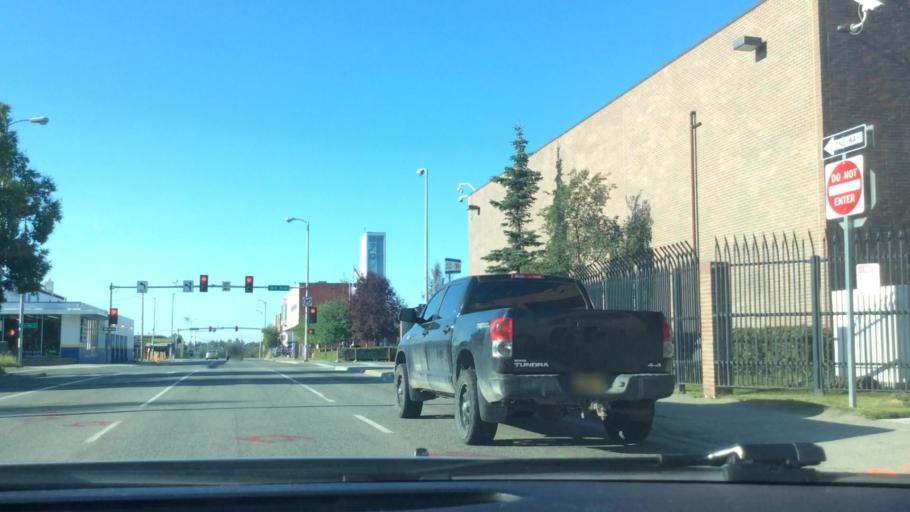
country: US
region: Alaska
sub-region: Anchorage Municipality
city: Anchorage
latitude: 61.2170
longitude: -149.8832
